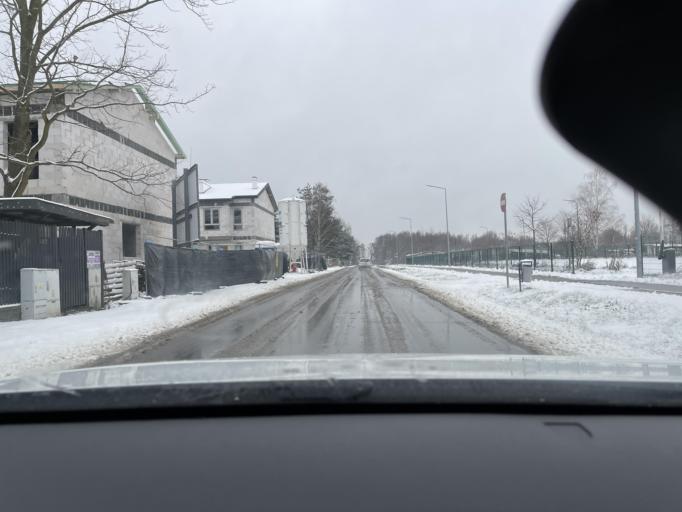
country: PL
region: Masovian Voivodeship
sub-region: Powiat zyrardowski
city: Zyrardow
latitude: 52.0357
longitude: 20.4521
